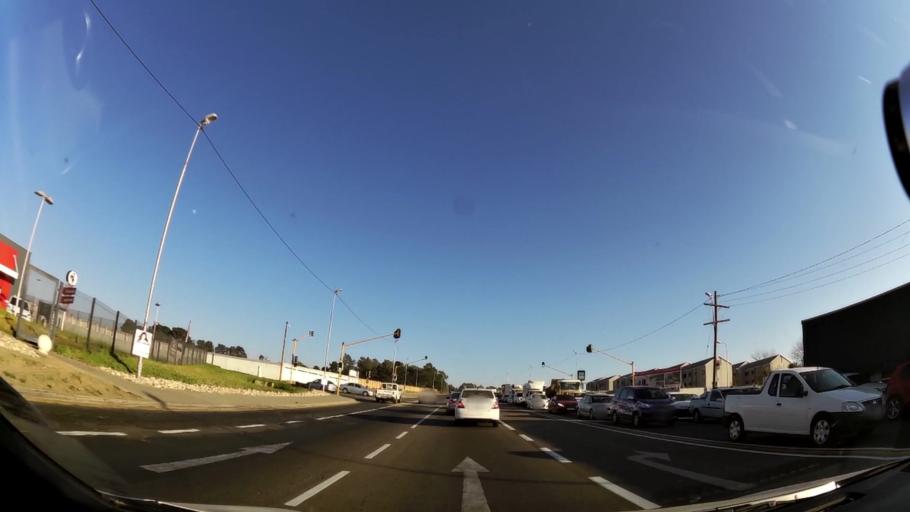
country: ZA
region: Gauteng
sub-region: City of Johannesburg Metropolitan Municipality
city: Midrand
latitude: -25.9436
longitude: 28.1062
